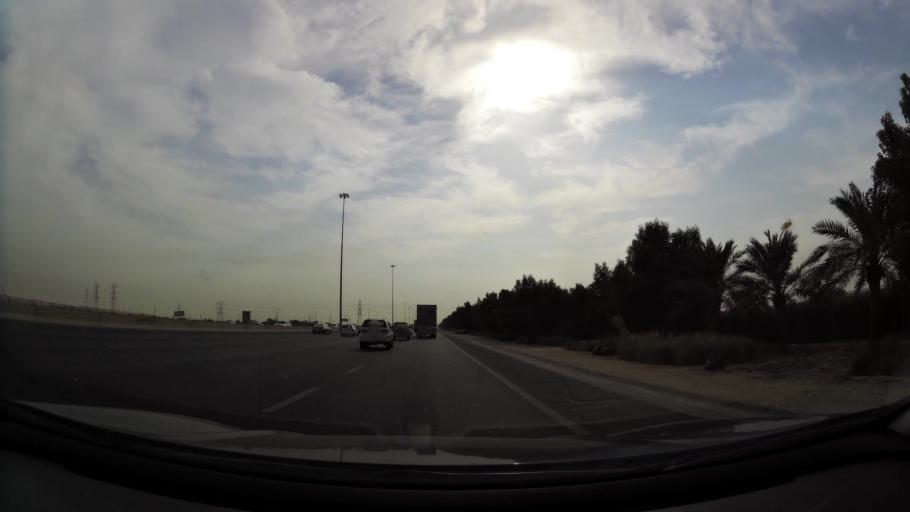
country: KW
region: Muhafazat al Jahra'
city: Al Jahra'
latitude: 29.3207
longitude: 47.7568
